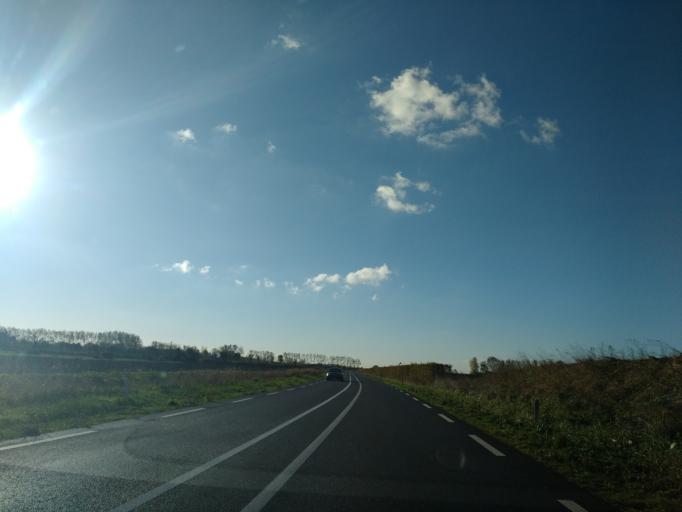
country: NL
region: Zeeland
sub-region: Gemeente Sluis
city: Sluis
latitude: 51.3280
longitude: 3.4754
